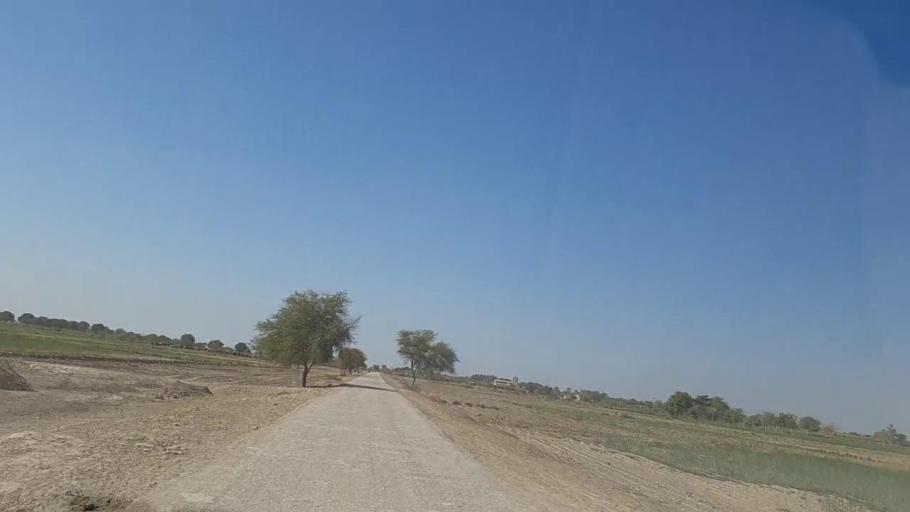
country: PK
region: Sindh
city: Digri
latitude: 25.1210
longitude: 69.0778
